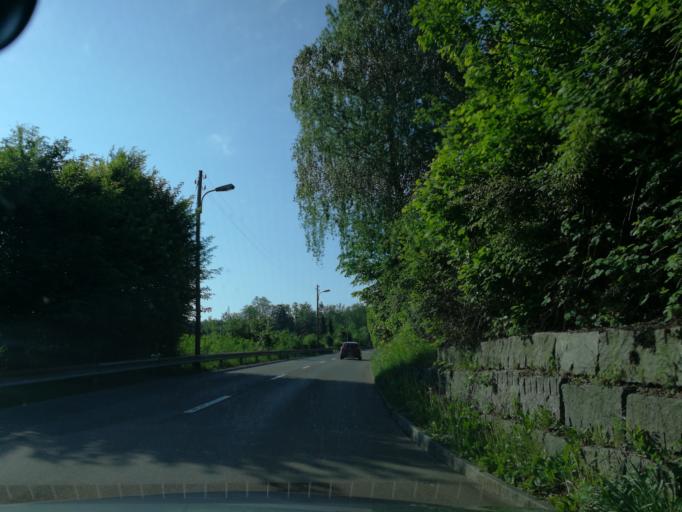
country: CH
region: Zurich
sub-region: Bezirk Horgen
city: Horgen / Allmend
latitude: 47.2526
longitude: 8.6074
